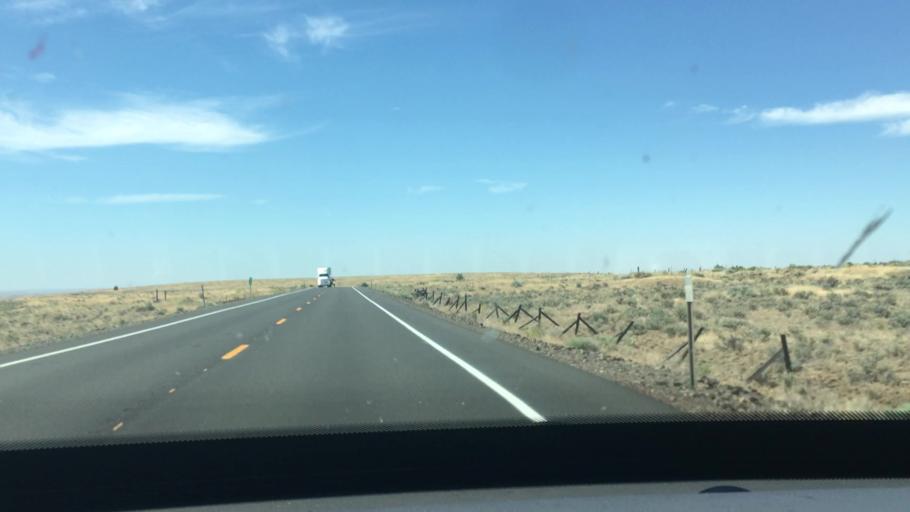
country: US
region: Oregon
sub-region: Sherman County
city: Moro
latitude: 45.0679
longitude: -120.6822
